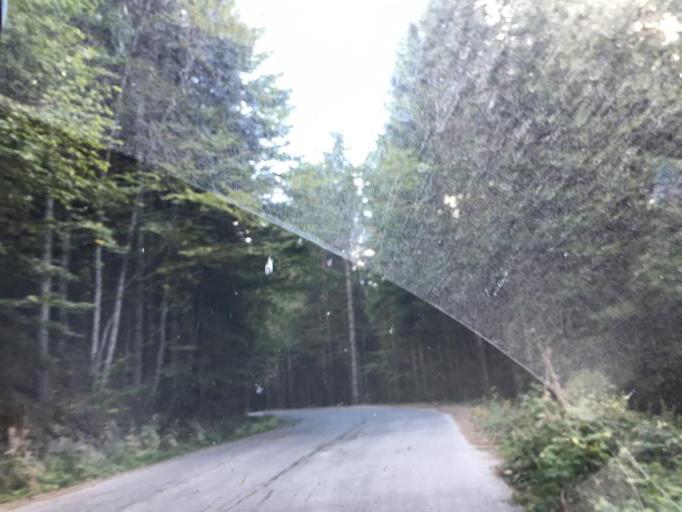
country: BG
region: Pazardzhik
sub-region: Obshtina Batak
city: Batak
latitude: 41.9182
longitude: 24.2831
